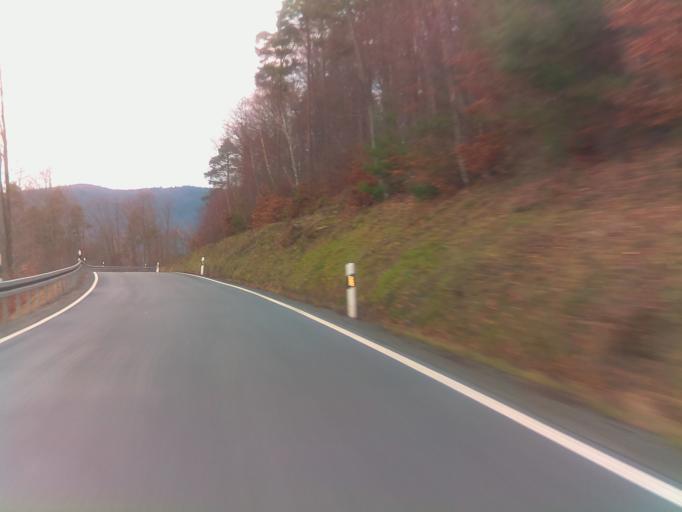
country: DE
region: Bavaria
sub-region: Regierungsbezirk Unterfranken
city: Miltenberg
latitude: 49.6951
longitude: 9.2843
